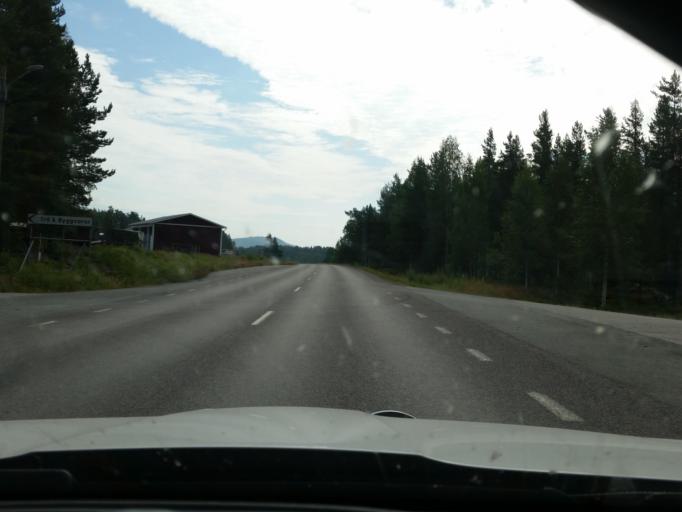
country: SE
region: Norrbotten
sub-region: Alvsbyns Kommun
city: AElvsbyn
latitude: 65.6753
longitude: 20.8360
